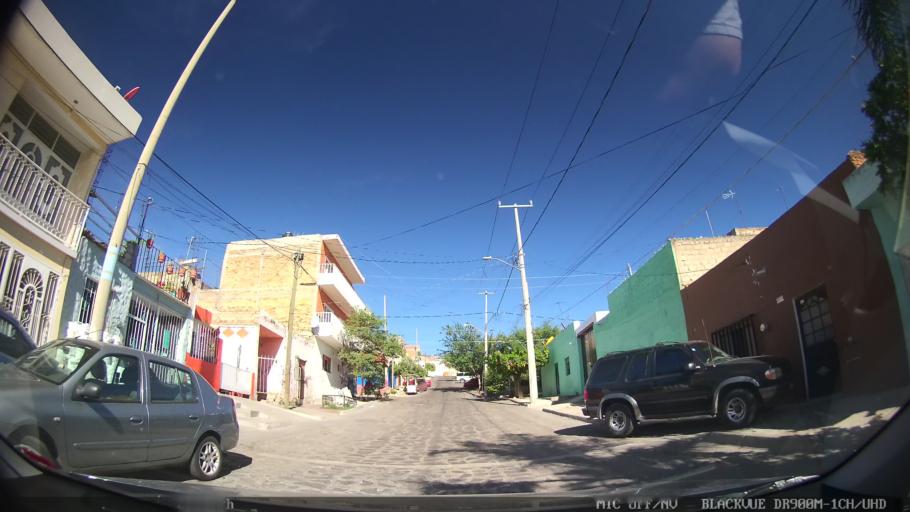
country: MX
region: Jalisco
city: Tlaquepaque
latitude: 20.6898
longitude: -103.2756
